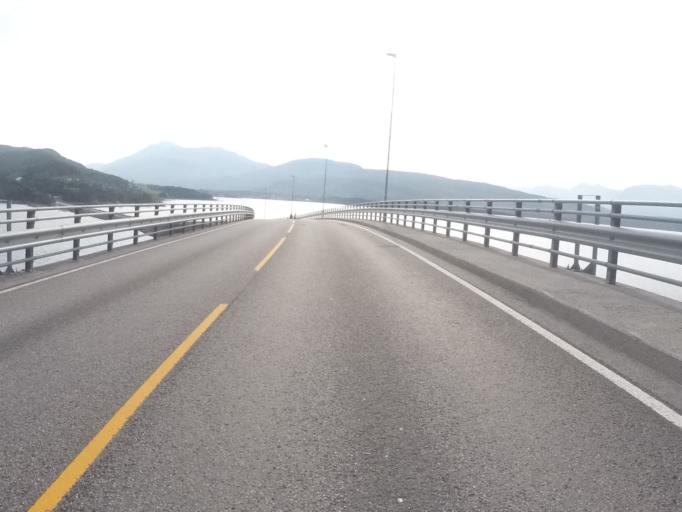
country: NO
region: More og Romsdal
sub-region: Molde
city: Hjelset
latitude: 62.7306
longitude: 7.3549
